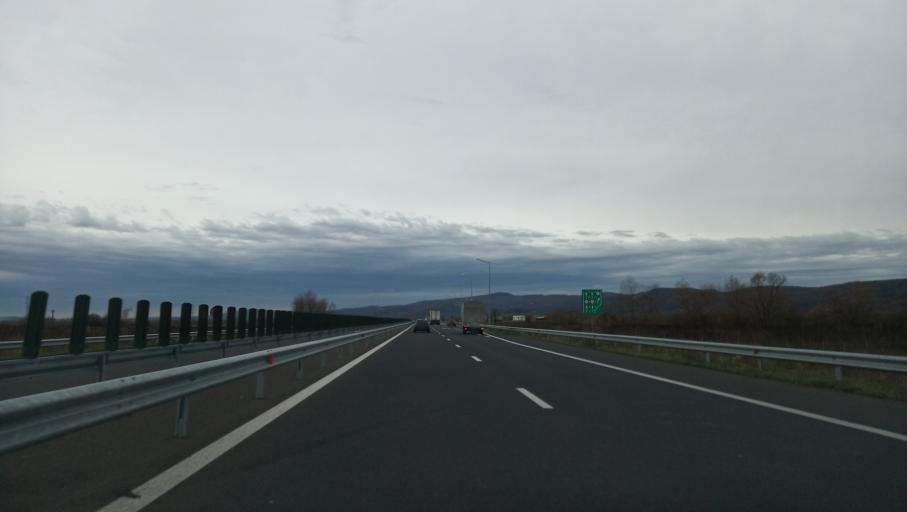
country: RO
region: Hunedoara
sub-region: Comuna Ilia
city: Ilia
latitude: 45.9474
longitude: 22.6607
